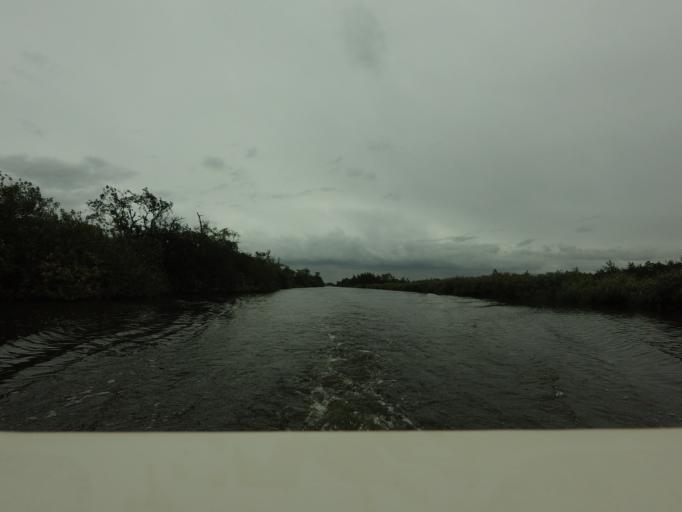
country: NL
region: Friesland
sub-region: Gemeente Boarnsterhim
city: Warten
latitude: 53.1204
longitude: 5.9298
